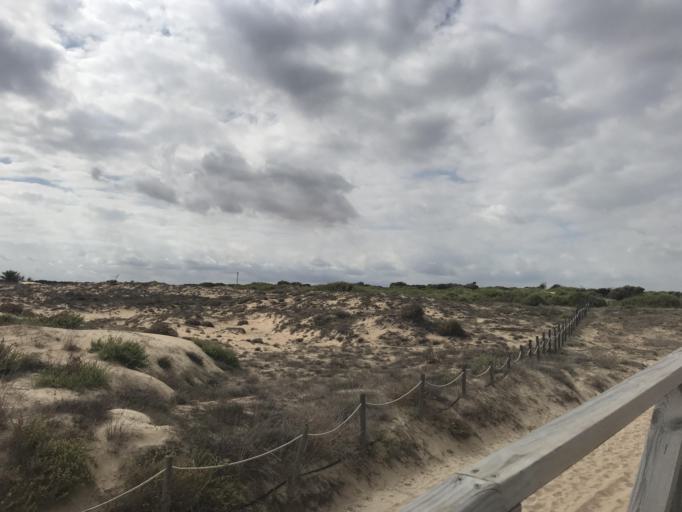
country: ES
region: Valencia
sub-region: Provincia de Alicante
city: Guardamar del Segura
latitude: 38.0470
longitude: -0.6518
